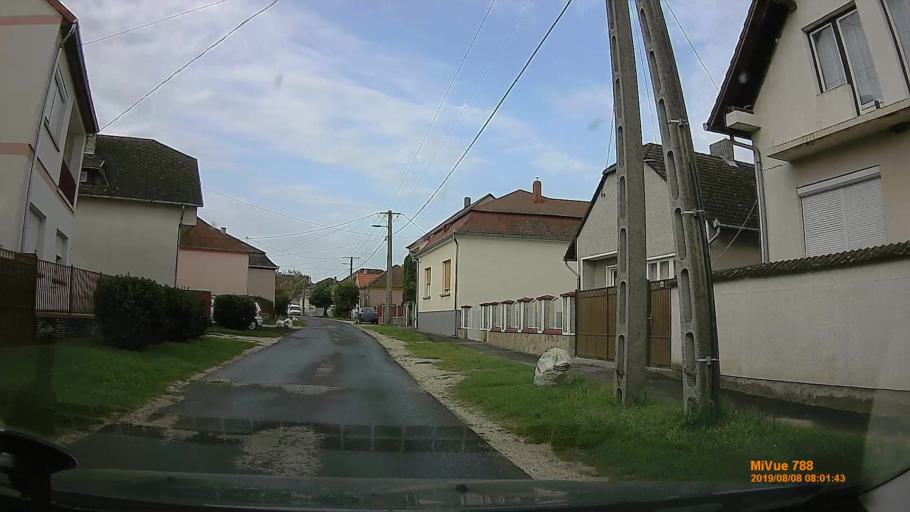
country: HU
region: Zala
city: Nagykanizsa
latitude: 46.4593
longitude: 16.9561
